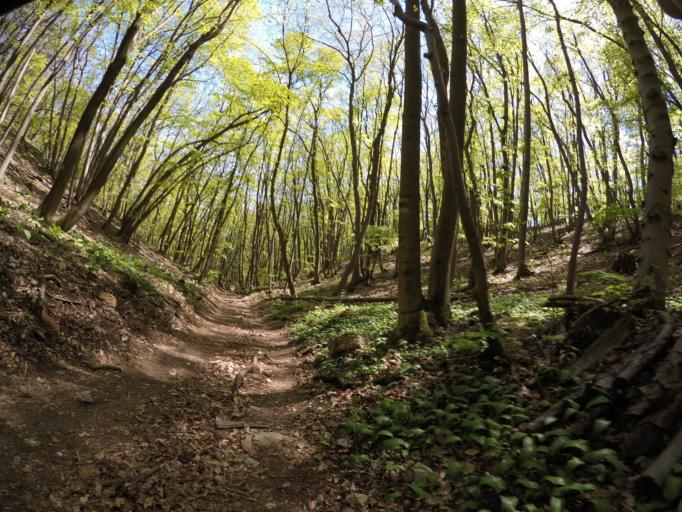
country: AT
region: Lower Austria
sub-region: Politischer Bezirk Modling
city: Gumpoldskirchen
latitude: 48.0481
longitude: 16.2597
